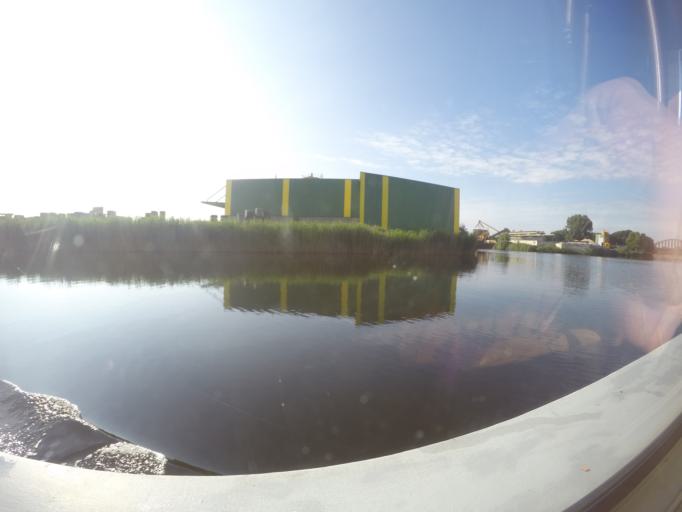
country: NL
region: Overijssel
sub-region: Gemeente Wierden
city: Wierden
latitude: 52.3661
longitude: 6.6238
